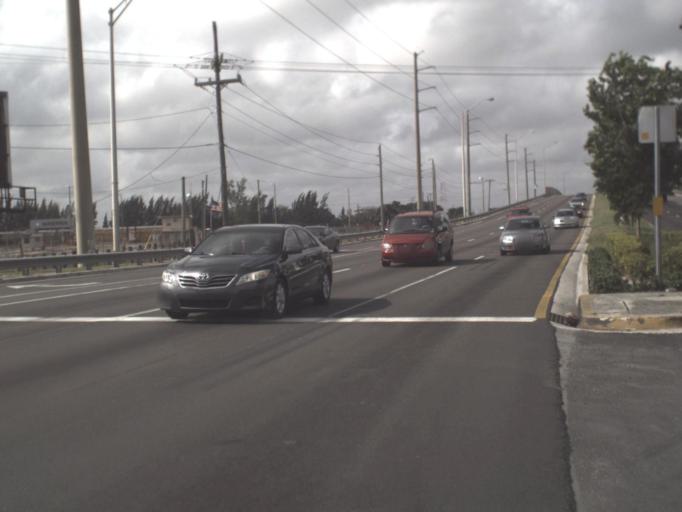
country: US
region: Florida
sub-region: Miami-Dade County
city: Virginia Gardens
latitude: 25.8074
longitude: -80.3051
